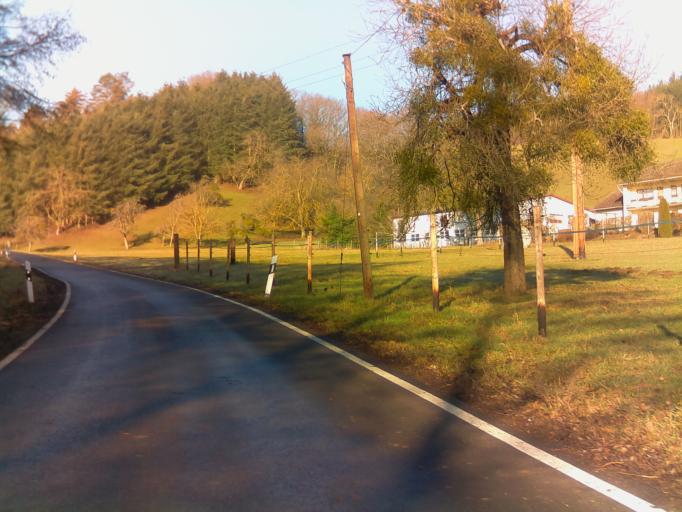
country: DE
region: Rheinland-Pfalz
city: Martinstein
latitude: 49.8103
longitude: 7.5519
